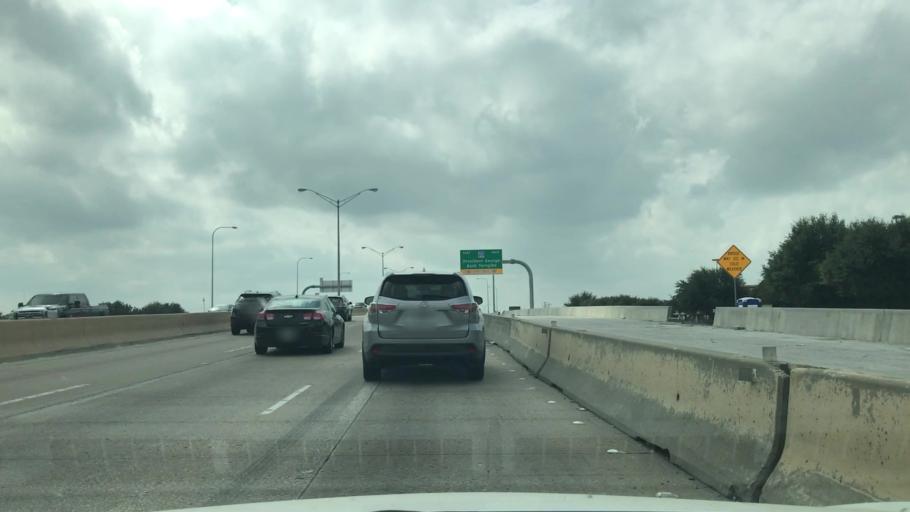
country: US
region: Texas
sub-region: Dallas County
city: Addison
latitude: 33.0305
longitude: -96.8293
